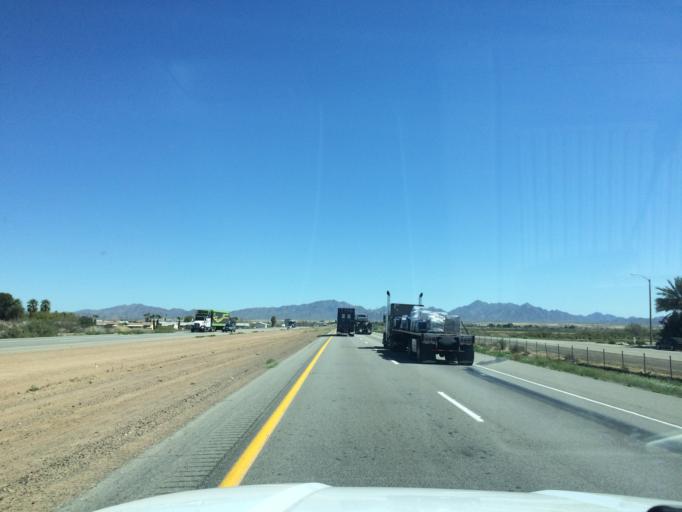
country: US
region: California
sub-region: Riverside County
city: Blythe
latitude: 33.6075
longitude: -114.5632
